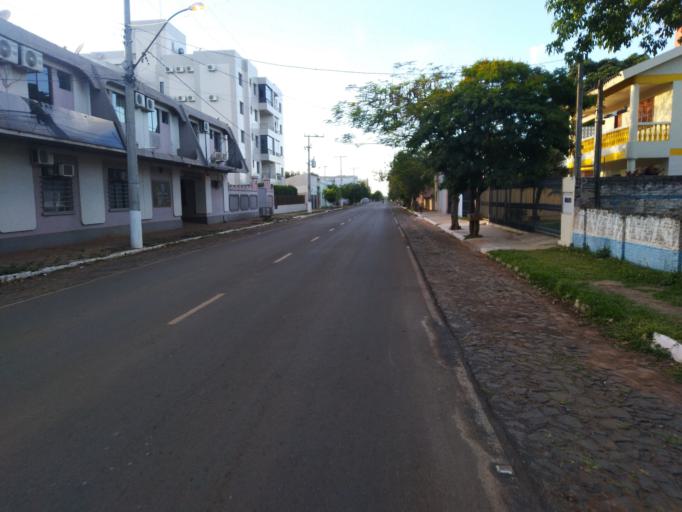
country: BR
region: Rio Grande do Sul
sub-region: Sao Borja
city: Sao Borja
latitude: -28.6604
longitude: -56.0090
